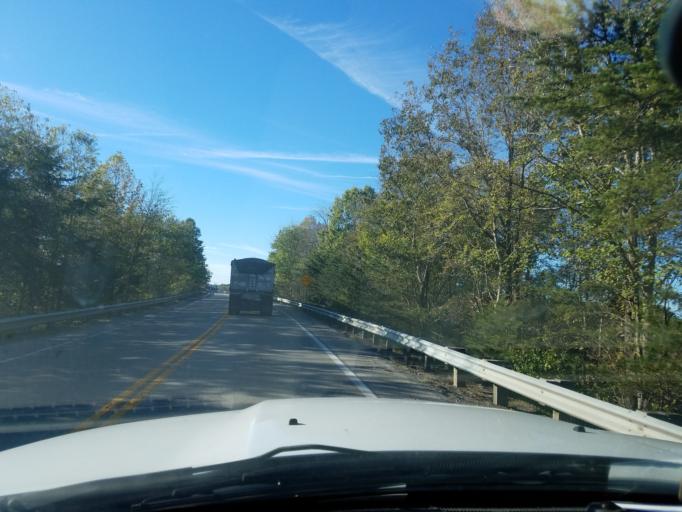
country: US
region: Kentucky
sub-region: Laurel County
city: London
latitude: 37.0630
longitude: -84.0545
